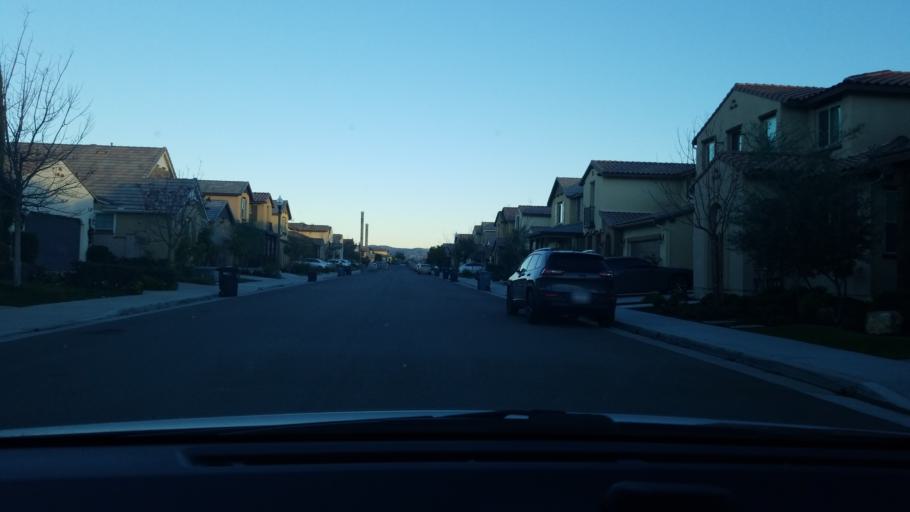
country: US
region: California
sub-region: Riverside County
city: Murrieta Hot Springs
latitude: 33.5527
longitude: -117.1069
